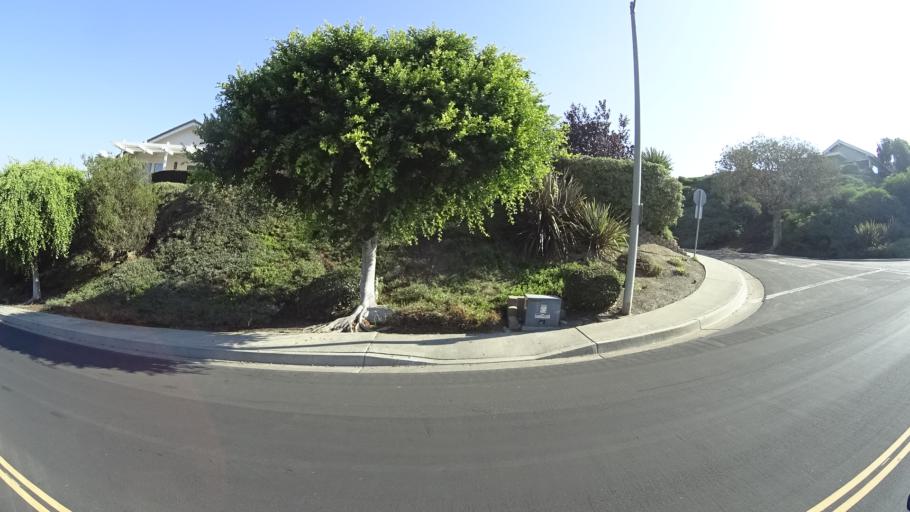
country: US
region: California
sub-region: Orange County
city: San Clemente
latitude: 33.4362
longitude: -117.6122
